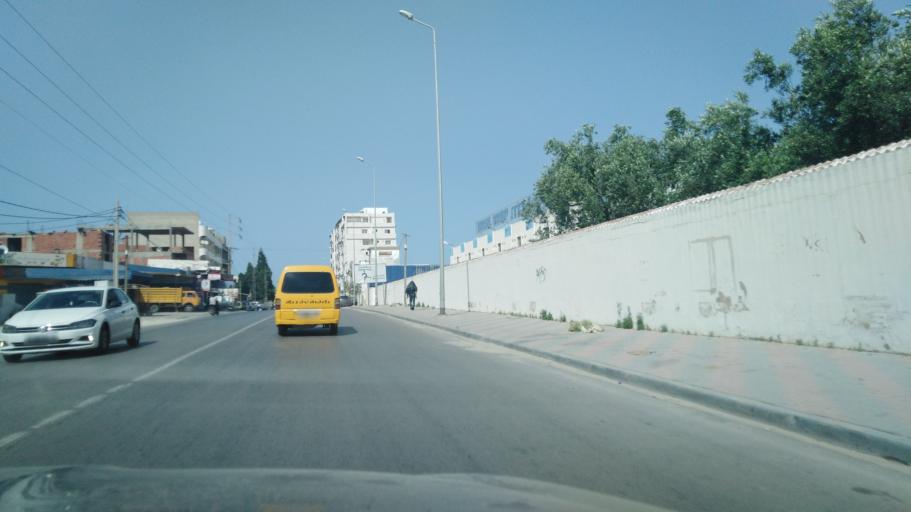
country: TN
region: Susah
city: Sousse
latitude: 35.8066
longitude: 10.6193
